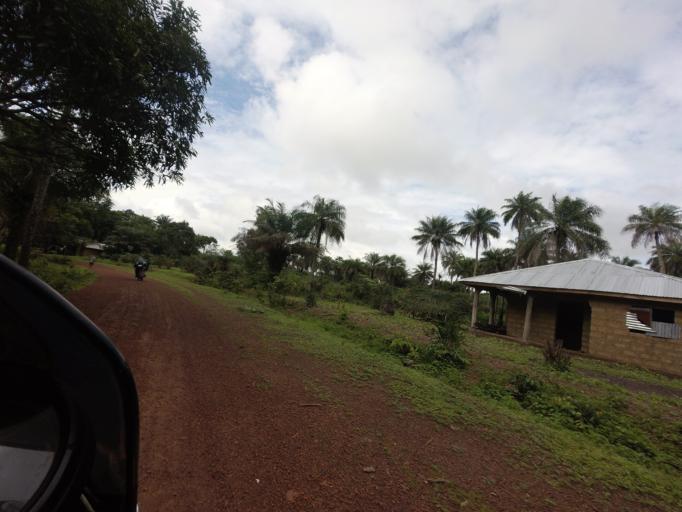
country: SL
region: Northern Province
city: Mambolo
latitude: 8.9790
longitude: -12.9996
